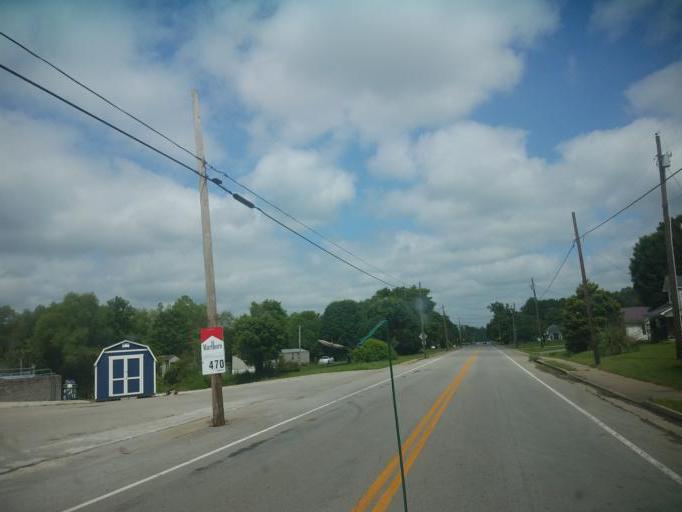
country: US
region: Kentucky
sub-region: Cumberland County
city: Burkesville
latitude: 36.8281
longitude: -85.5084
